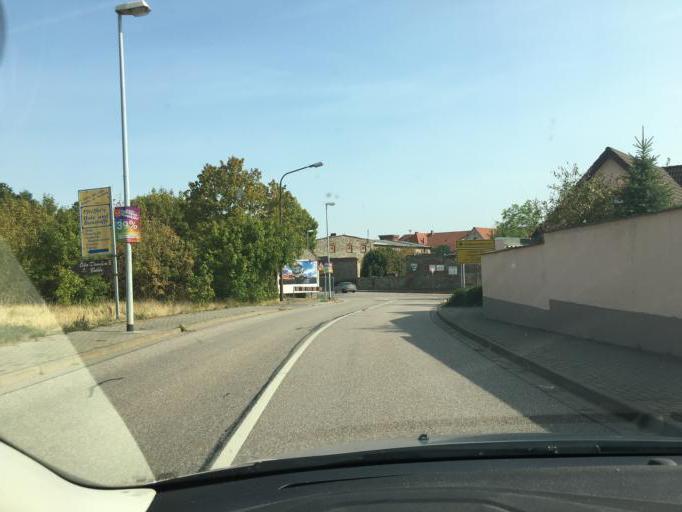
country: DE
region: Saxony-Anhalt
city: Wulfen
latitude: 51.7850
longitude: 11.8834
